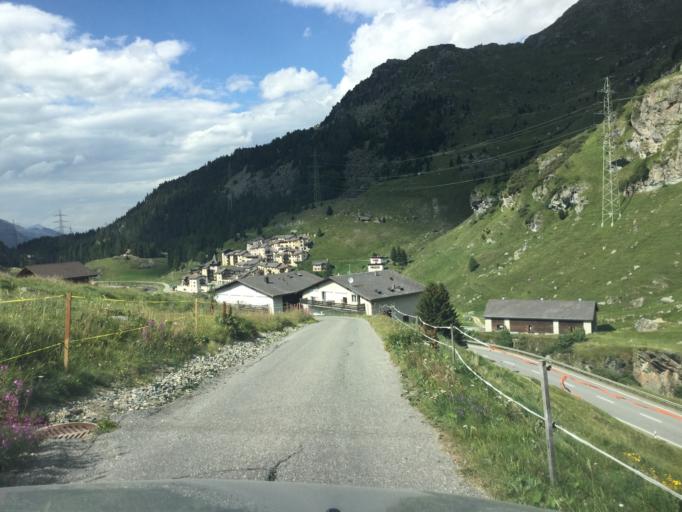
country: CH
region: Grisons
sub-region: Maloja District
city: Silvaplana
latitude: 46.4653
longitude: 9.6528
